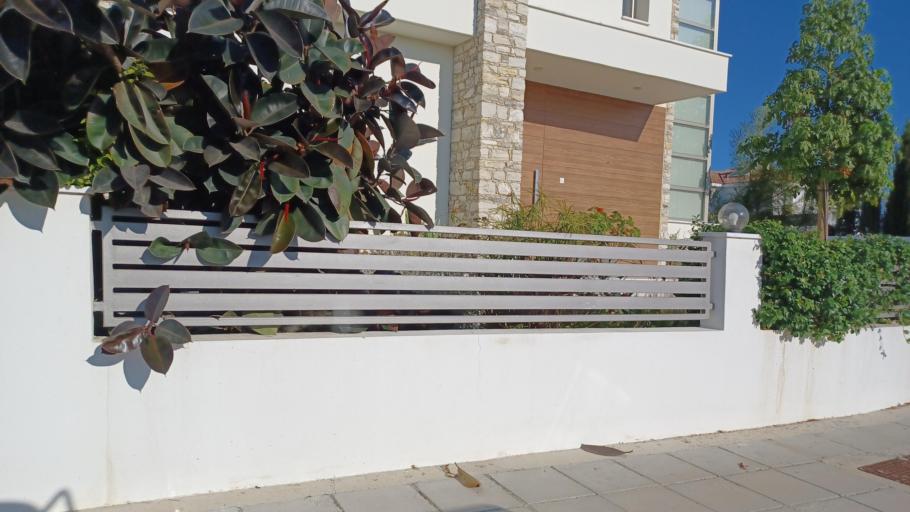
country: CY
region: Larnaka
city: Voroklini
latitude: 34.9832
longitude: 33.6794
